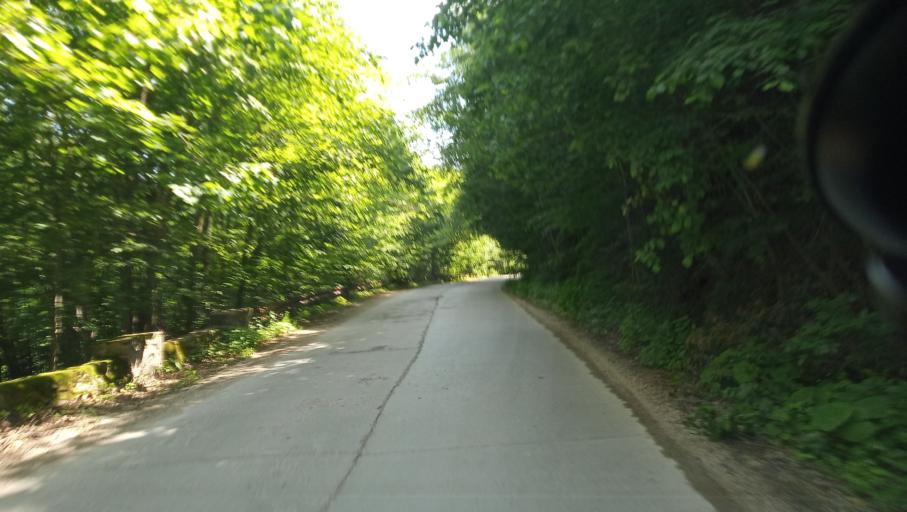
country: RO
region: Cluj
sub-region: Comuna Capusu Mare
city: Capusu Mare
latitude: 46.7098
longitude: 23.2560
